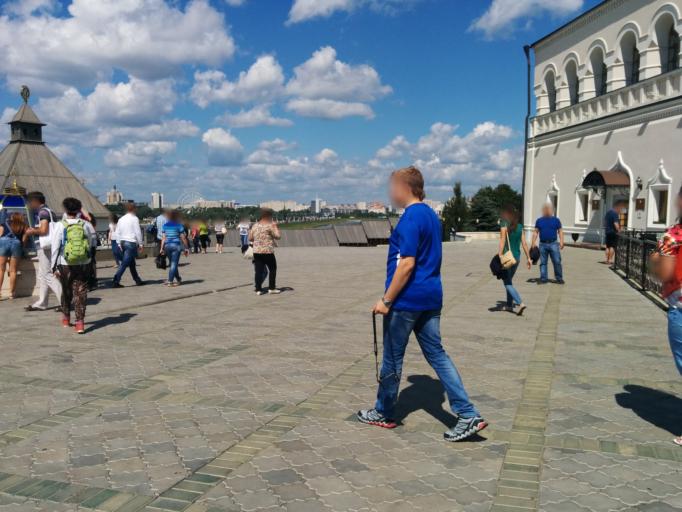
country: RU
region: Tatarstan
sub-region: Gorod Kazan'
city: Kazan
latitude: 55.8005
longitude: 49.1048
